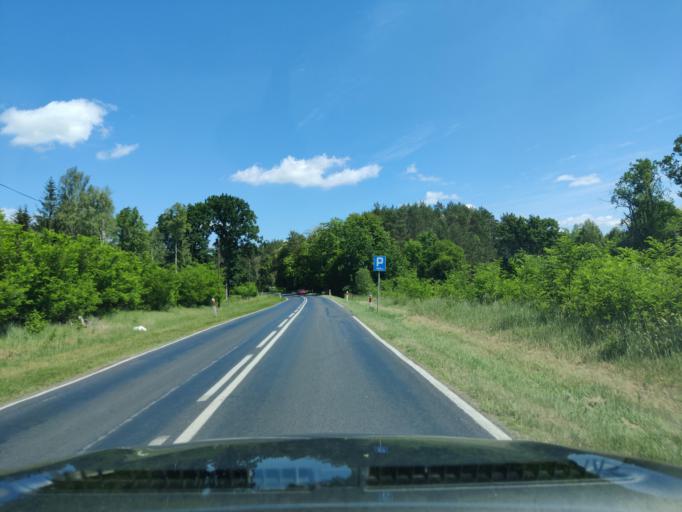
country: PL
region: Greater Poland Voivodeship
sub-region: Powiat nowotomyski
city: Nowy Tomysl
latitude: 52.2328
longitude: 16.1156
